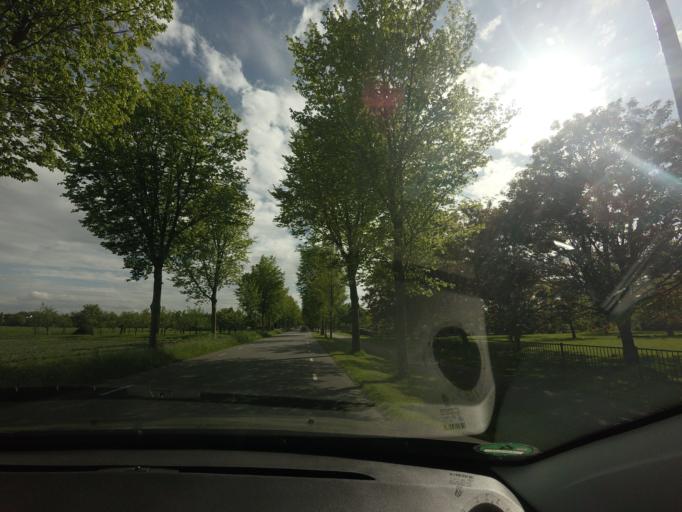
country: NL
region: North Holland
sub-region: Gemeente Beemster
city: Halfweg
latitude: 52.5534
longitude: 4.9158
